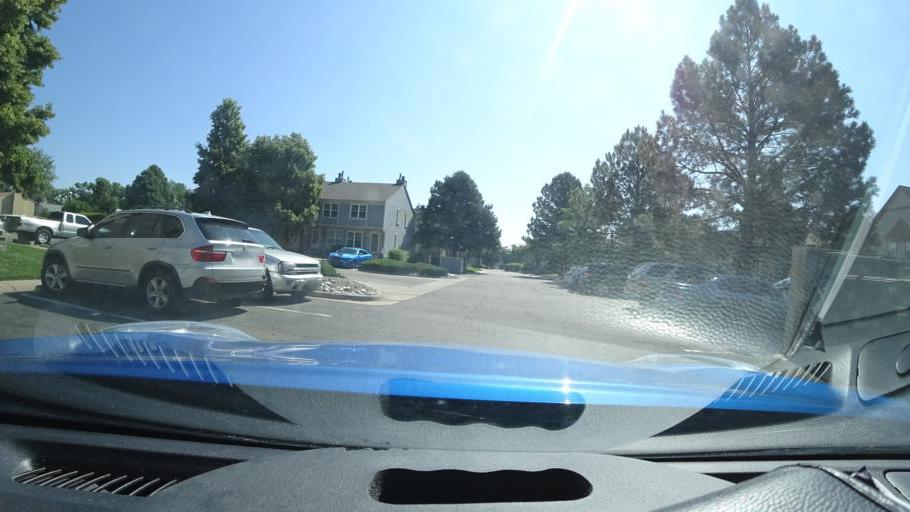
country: US
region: Colorado
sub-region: Adams County
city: Aurora
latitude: 39.6863
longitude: -104.8226
